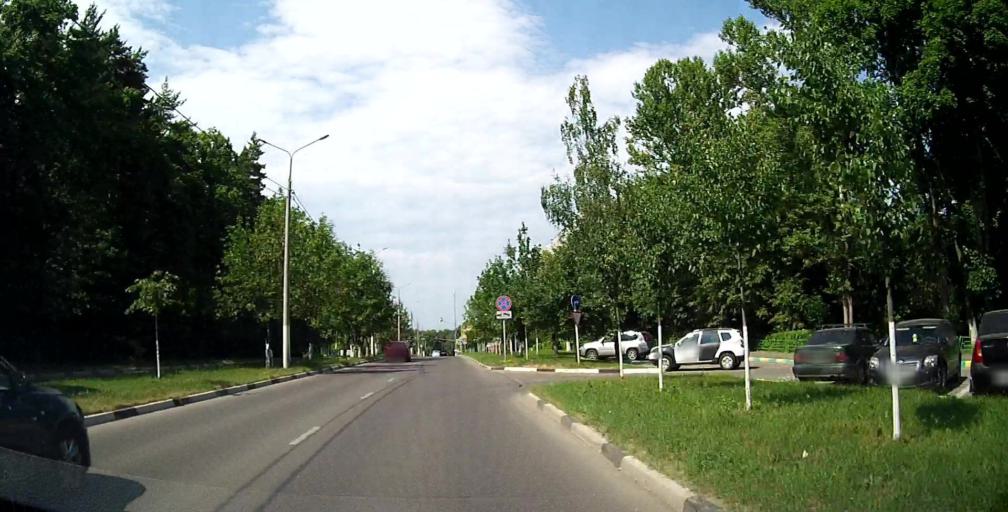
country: RU
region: Moskovskaya
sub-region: Podol'skiy Rayon
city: Podol'sk
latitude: 55.4161
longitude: 37.5211
